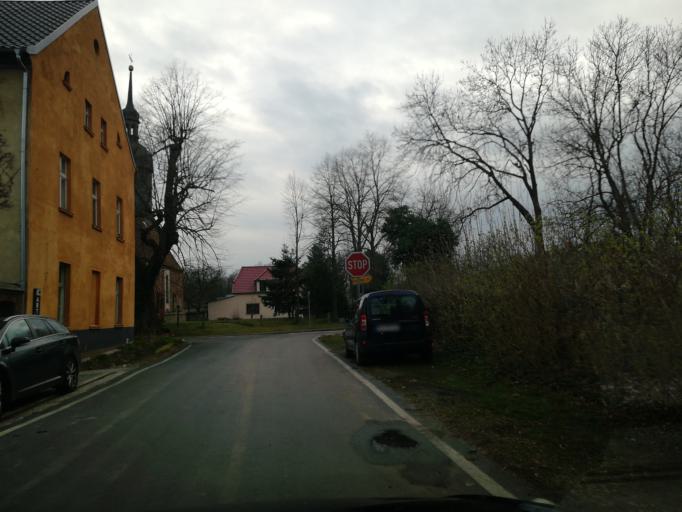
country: DE
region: Brandenburg
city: Vetschau
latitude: 51.7130
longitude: 14.0891
